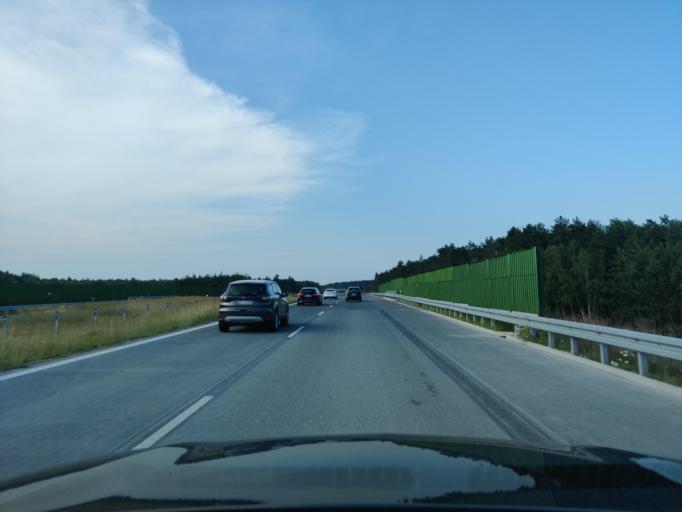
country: PL
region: Masovian Voivodeship
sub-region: Powiat mlawski
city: Strzegowo
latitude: 52.9062
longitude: 20.2753
